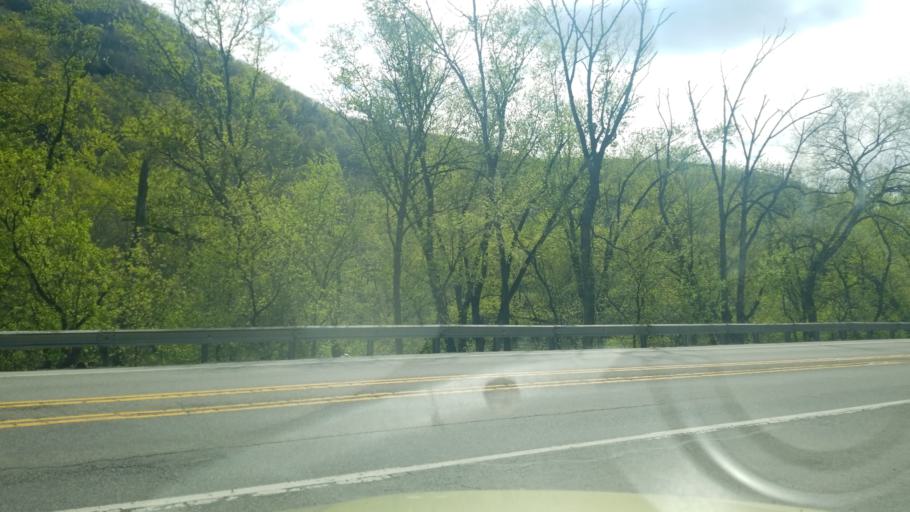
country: US
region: Pennsylvania
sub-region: Huntingdon County
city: Mount Union
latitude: 40.3918
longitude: -77.9145
